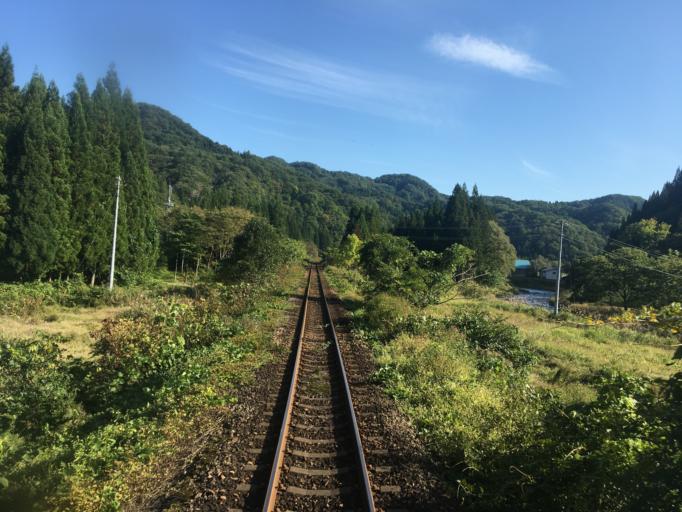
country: JP
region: Akita
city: Kakunodatemachi
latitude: 39.7787
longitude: 140.6018
